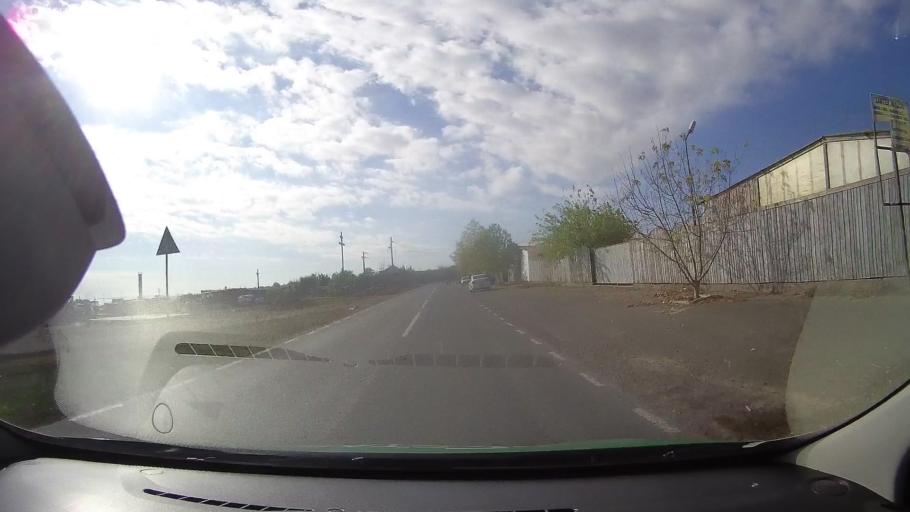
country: RO
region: Tulcea
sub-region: Comuna Sarichioi
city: Sarichioi
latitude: 44.9576
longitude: 28.8571
